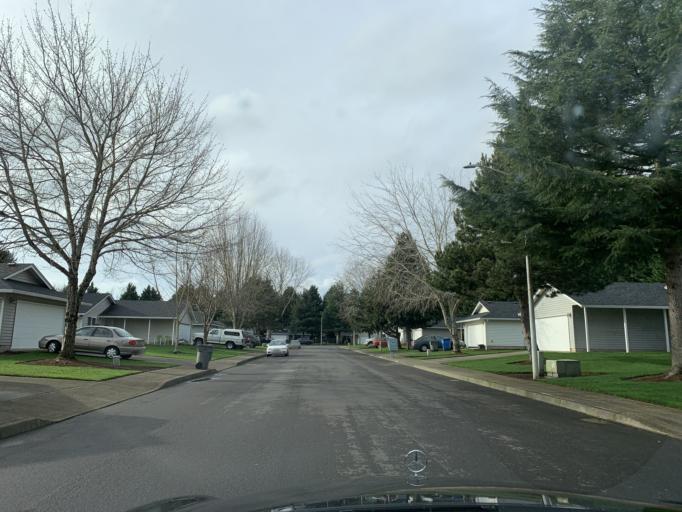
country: US
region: Washington
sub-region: Clark County
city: Mill Plain
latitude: 45.6222
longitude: -122.5142
